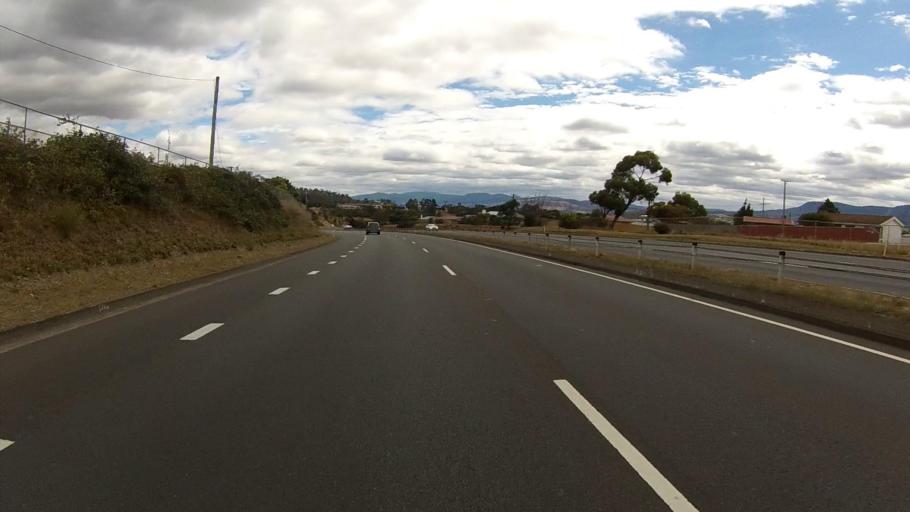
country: AU
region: Tasmania
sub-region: Glenorchy
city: Berriedale
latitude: -42.8036
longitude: 147.2497
